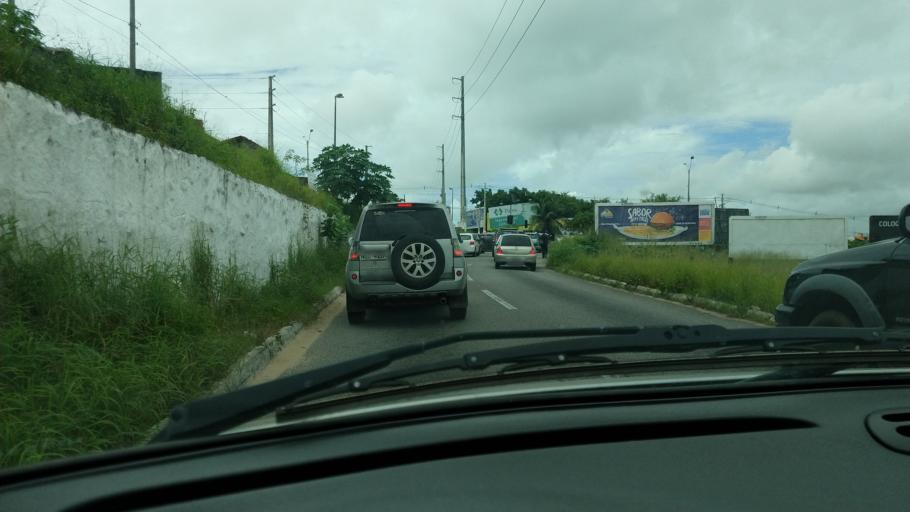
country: BR
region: Rio Grande do Norte
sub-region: Natal
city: Natal
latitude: -5.8409
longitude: -35.2219
